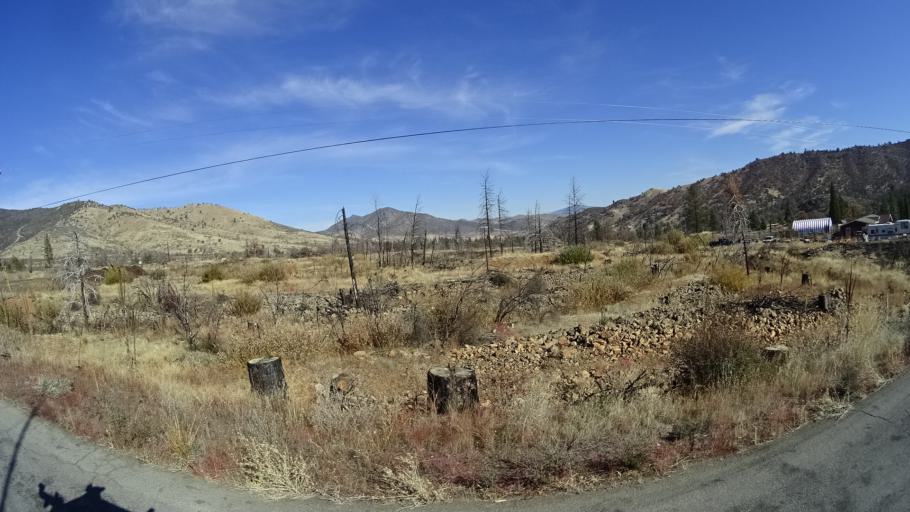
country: US
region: California
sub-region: Siskiyou County
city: Yreka
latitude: 41.7655
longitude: -122.6278
